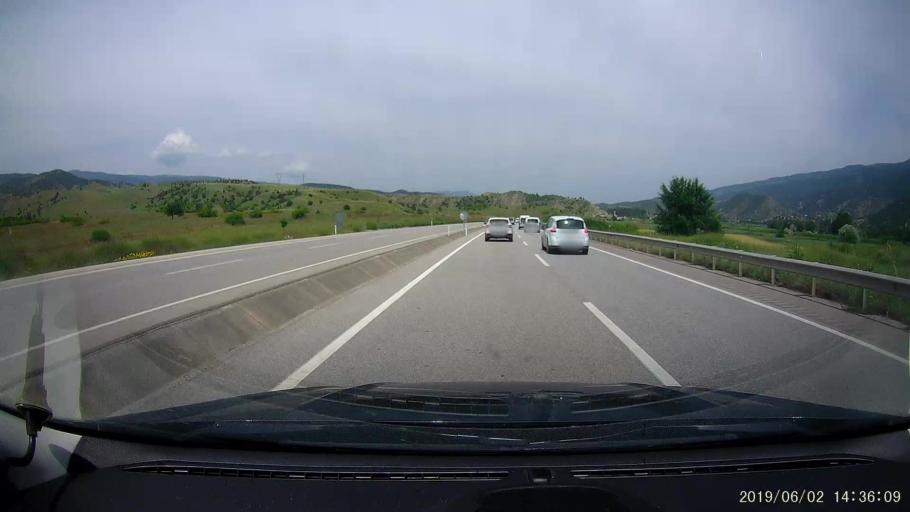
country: TR
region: Kastamonu
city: Tosya
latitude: 41.0454
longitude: 34.2294
